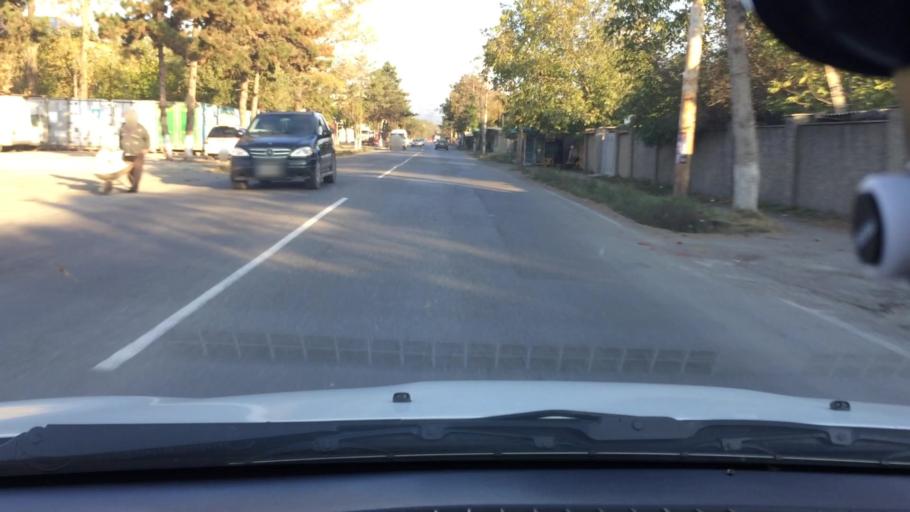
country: GE
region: Shida Kartli
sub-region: Khashuris Raioni
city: Khashuri
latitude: 41.9895
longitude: 43.5914
